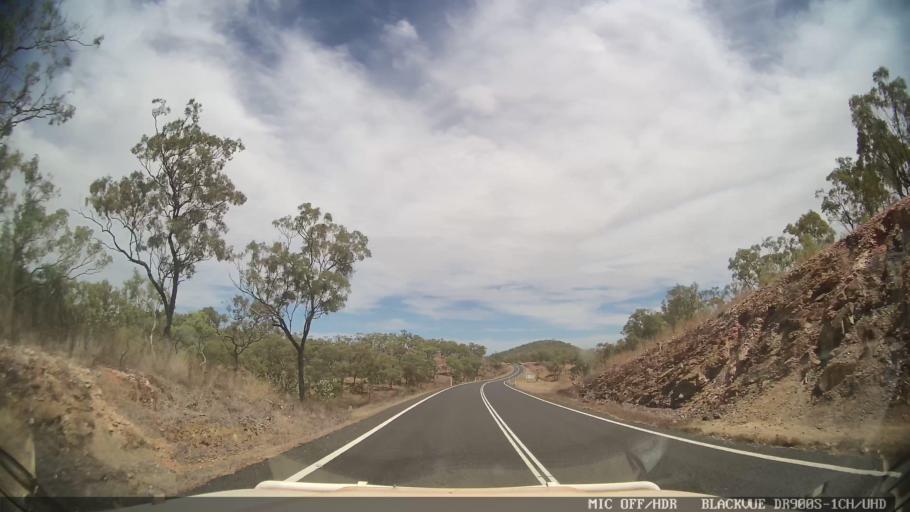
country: AU
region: Queensland
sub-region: Cairns
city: Port Douglas
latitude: -16.1499
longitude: 144.7662
